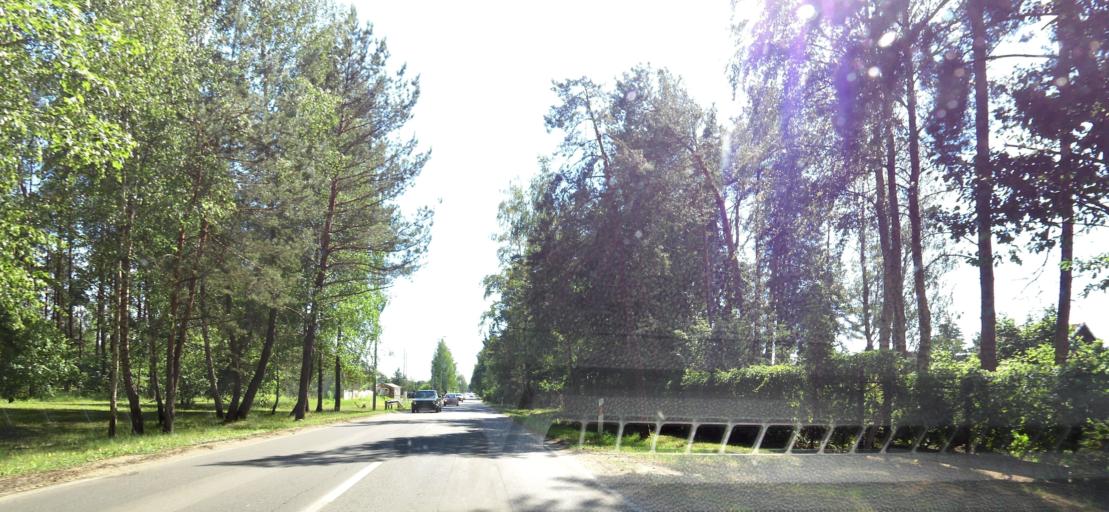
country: LT
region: Vilnius County
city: Rasos
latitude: 54.7870
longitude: 25.3483
